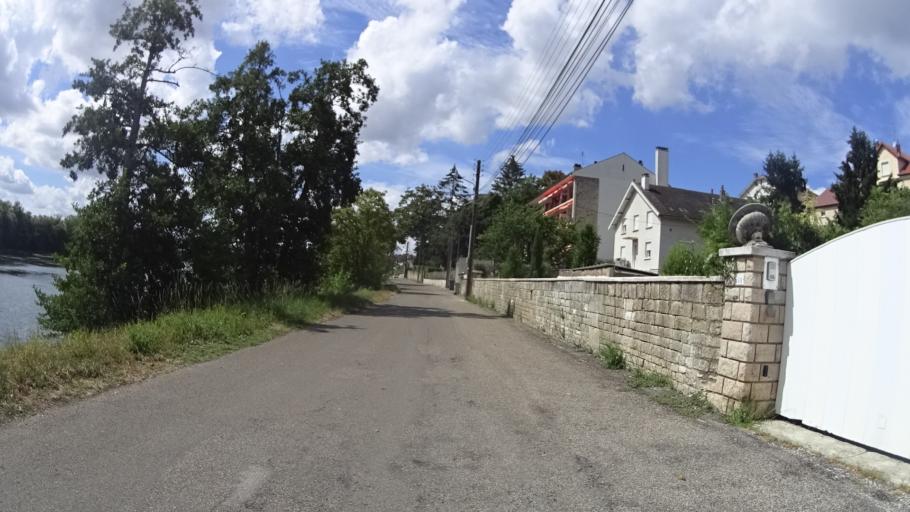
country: FR
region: Franche-Comte
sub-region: Departement du Jura
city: Dole
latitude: 47.0860
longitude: 5.4876
